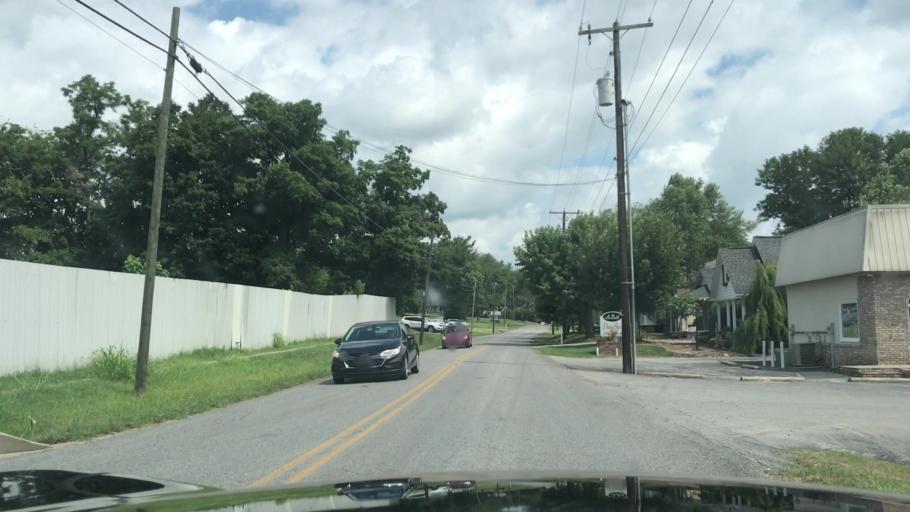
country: US
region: Kentucky
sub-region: Muhlenberg County
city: Greenville
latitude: 37.2150
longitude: -87.1796
